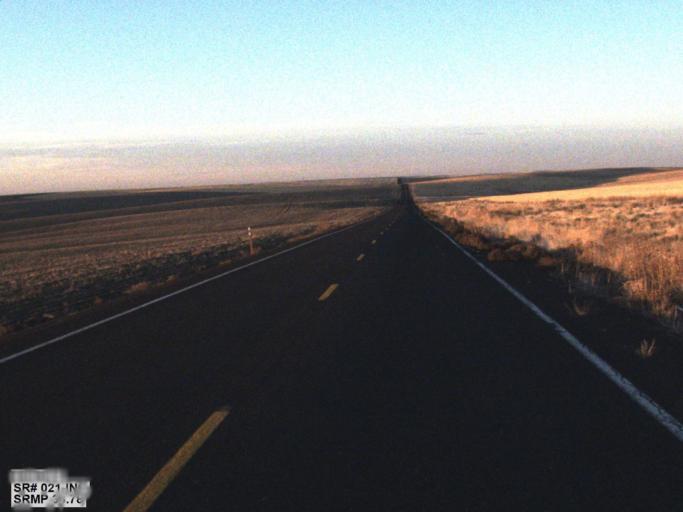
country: US
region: Washington
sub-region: Adams County
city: Ritzville
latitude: 47.0395
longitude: -118.6632
